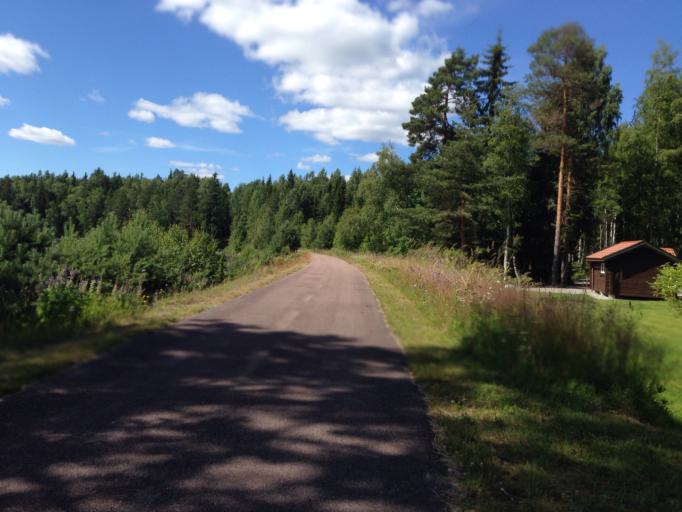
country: SE
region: Dalarna
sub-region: Ludvika Kommun
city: Grangesberg
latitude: 60.2127
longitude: 15.0478
